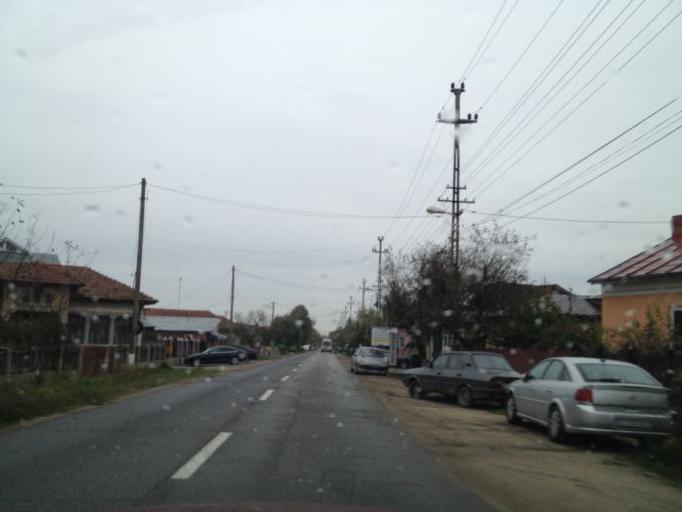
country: RO
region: Dolj
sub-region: Municipiul Craiova
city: Mofleni
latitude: 44.3025
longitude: 23.7574
